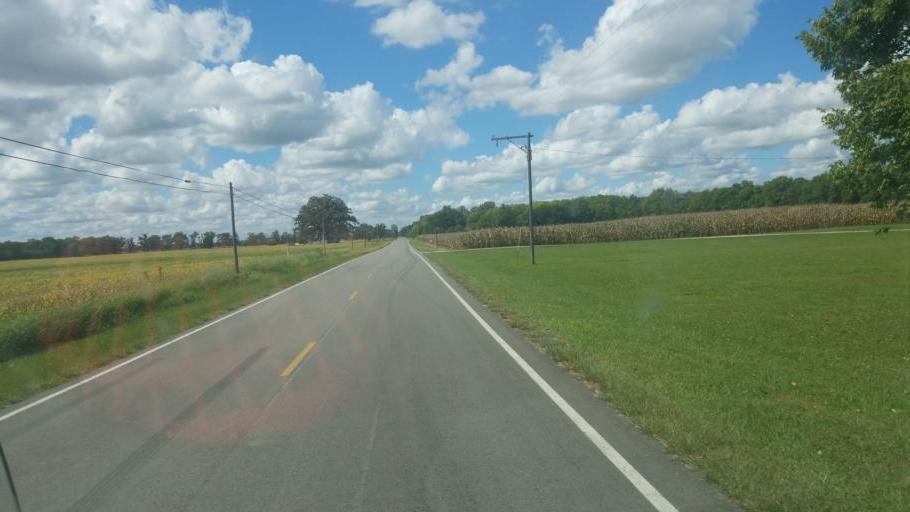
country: US
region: Ohio
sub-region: Champaign County
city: North Lewisburg
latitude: 40.1884
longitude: -83.4621
